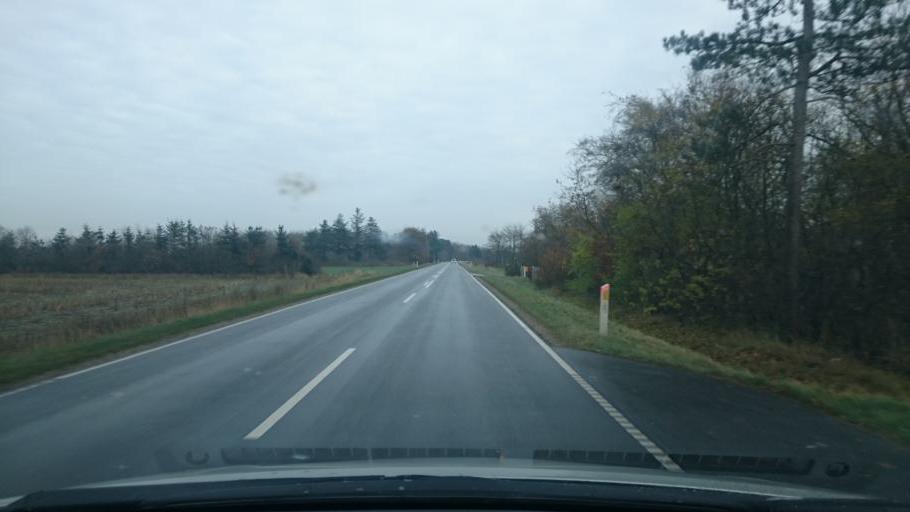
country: DK
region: South Denmark
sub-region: Esbjerg Kommune
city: Ribe
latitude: 55.3350
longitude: 8.8429
